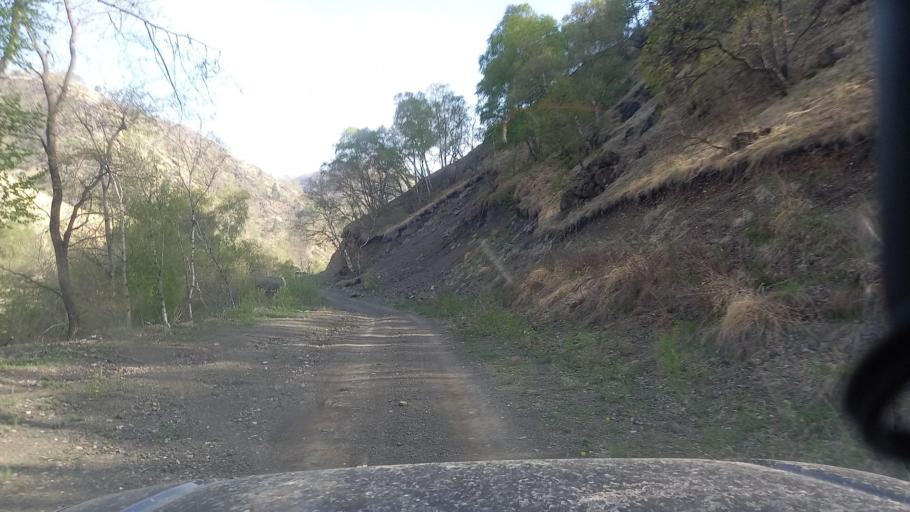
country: RU
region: Kabardino-Balkariya
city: Kamennomostskoye
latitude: 43.7186
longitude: 42.8441
